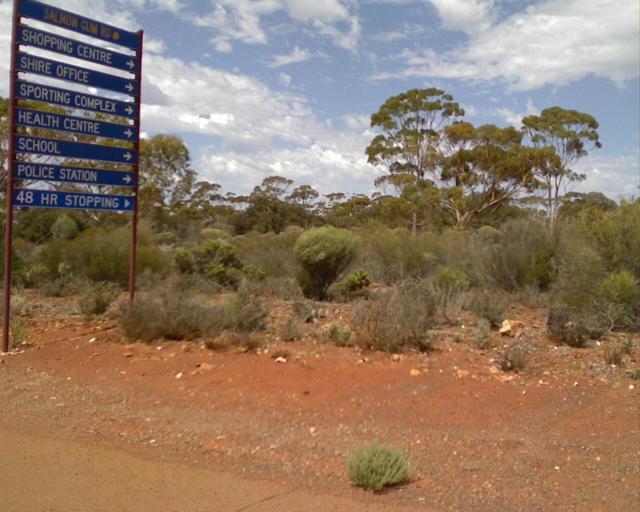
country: AU
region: Western Australia
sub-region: Kalgoorlie/Boulder
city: Stoneville
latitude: -31.2109
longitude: 121.6237
